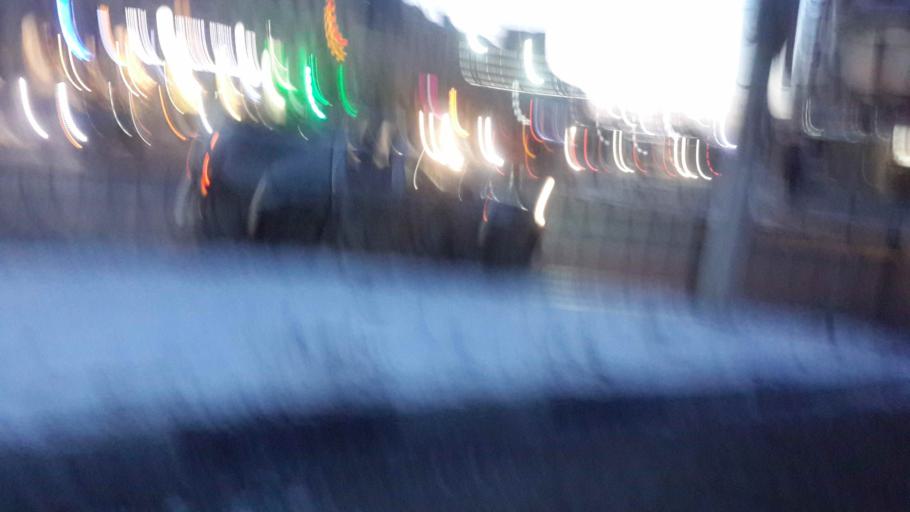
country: RU
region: Tula
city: Tula
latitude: 54.1972
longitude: 37.6014
